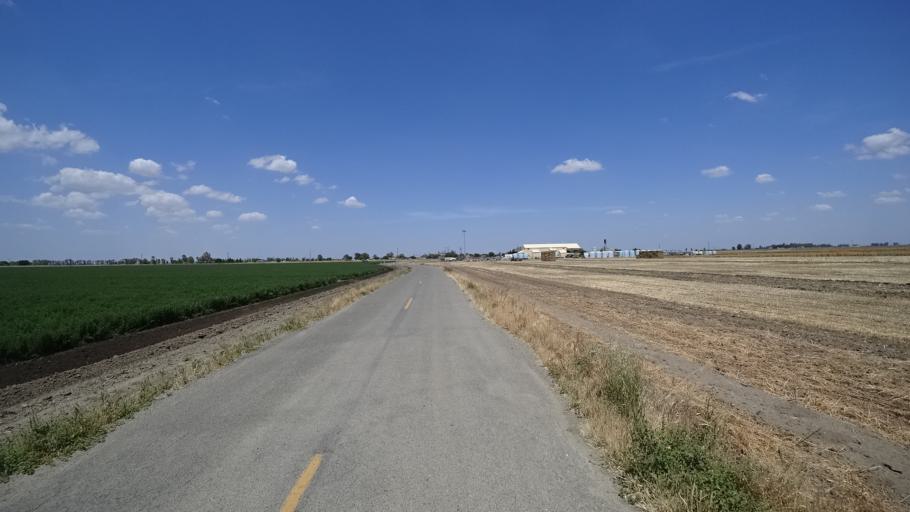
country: US
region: California
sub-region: Kings County
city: Stratford
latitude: 36.1789
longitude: -119.8250
